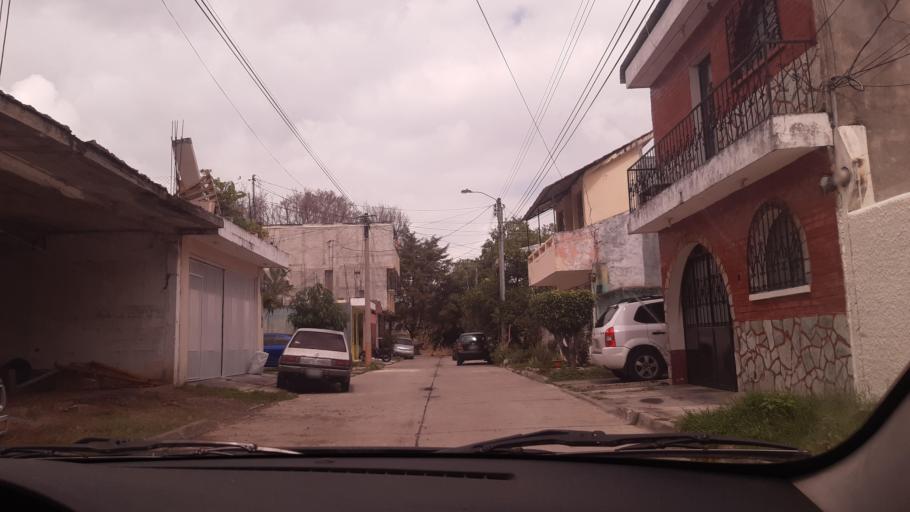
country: GT
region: Guatemala
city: Petapa
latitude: 14.5038
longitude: -90.5459
